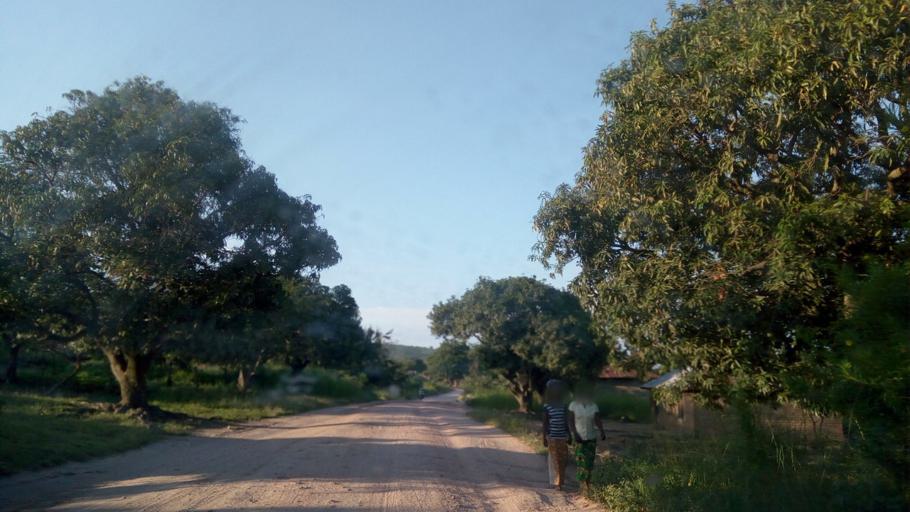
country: BI
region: Bururi
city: Rumonge
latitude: -4.1706
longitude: 29.0604
